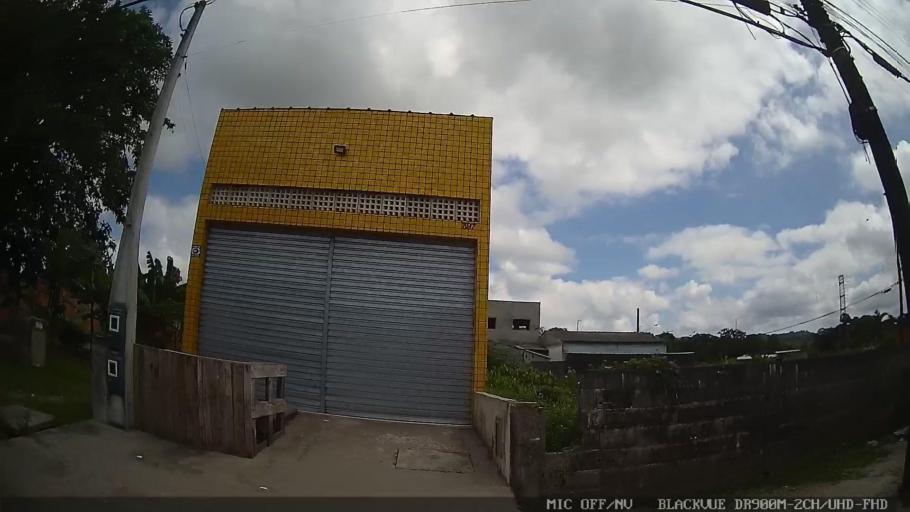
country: BR
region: Sao Paulo
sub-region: Peruibe
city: Peruibe
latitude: -24.2924
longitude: -47.0192
